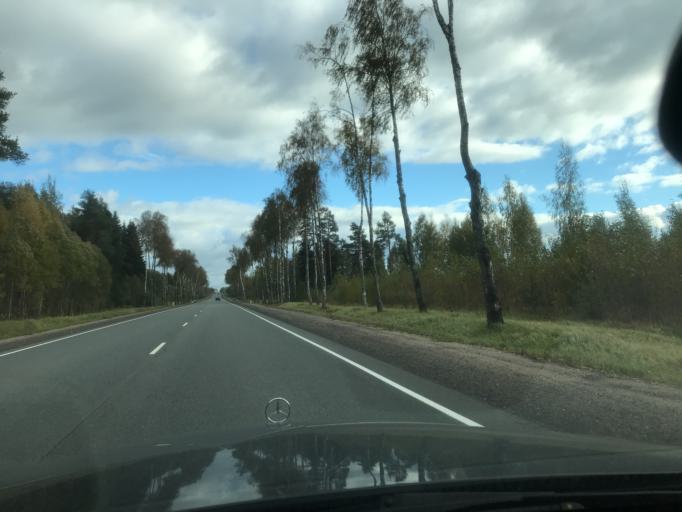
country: RU
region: Pskov
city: Opochka
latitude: 56.6782
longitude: 28.7144
